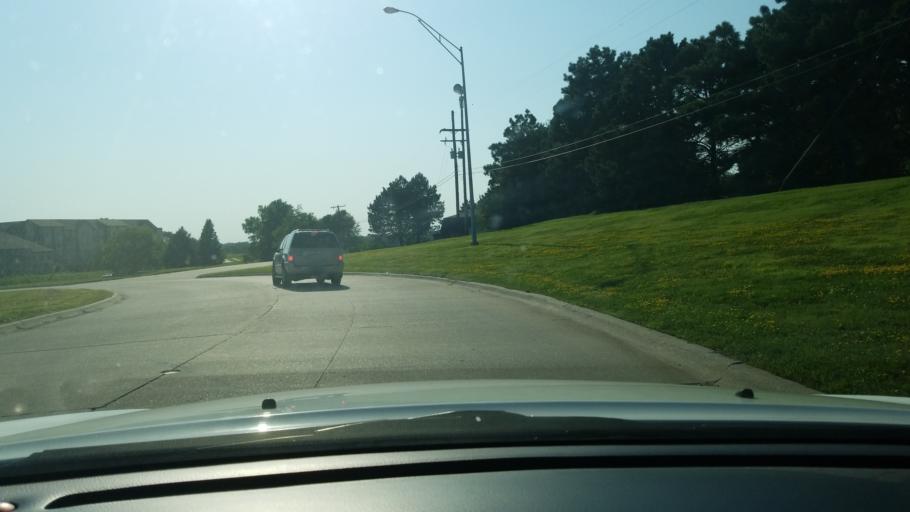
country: US
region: Nebraska
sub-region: Lancaster County
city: Lincoln
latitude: 40.7407
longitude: -96.6129
